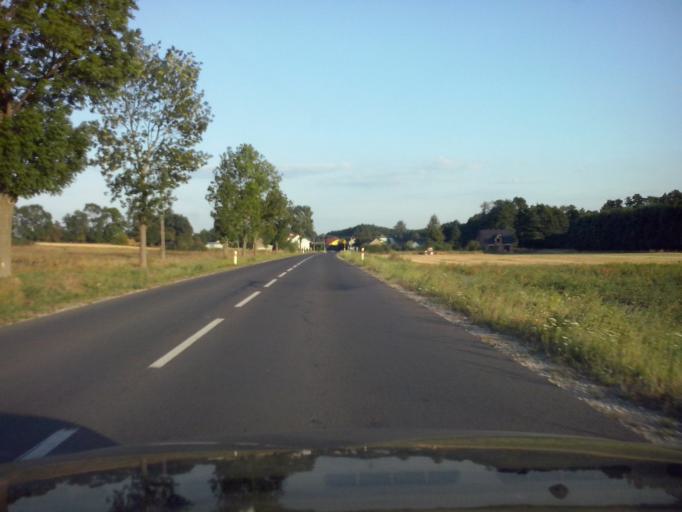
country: PL
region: Swietokrzyskie
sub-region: Powiat kielecki
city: Chmielnik
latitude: 50.6115
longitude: 20.7926
